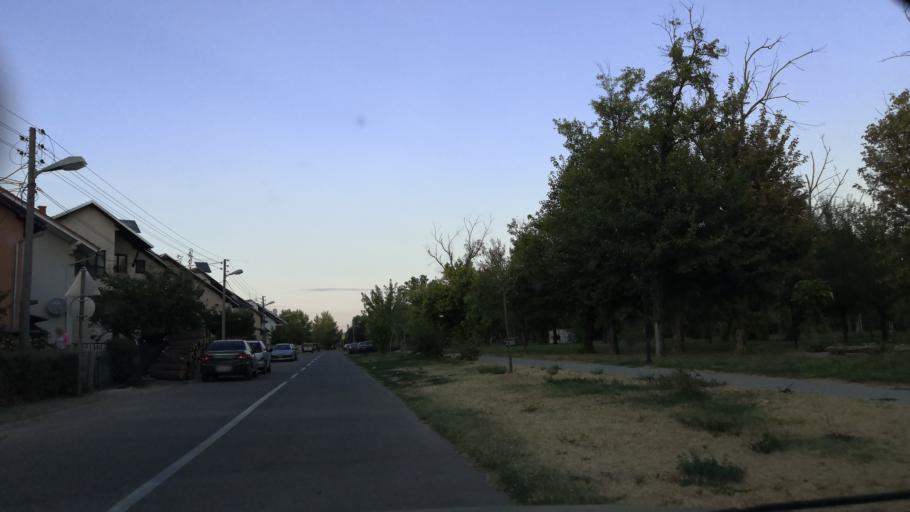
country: RS
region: Central Serbia
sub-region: Borski Okrug
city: Negotin
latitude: 44.2295
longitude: 22.5224
